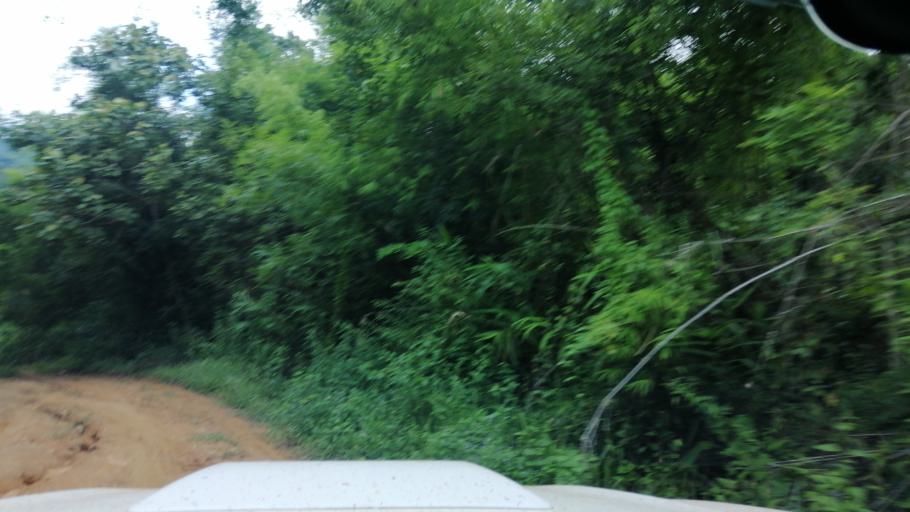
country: TH
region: Nan
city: Mae Charim
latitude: 18.7516
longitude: 101.2890
